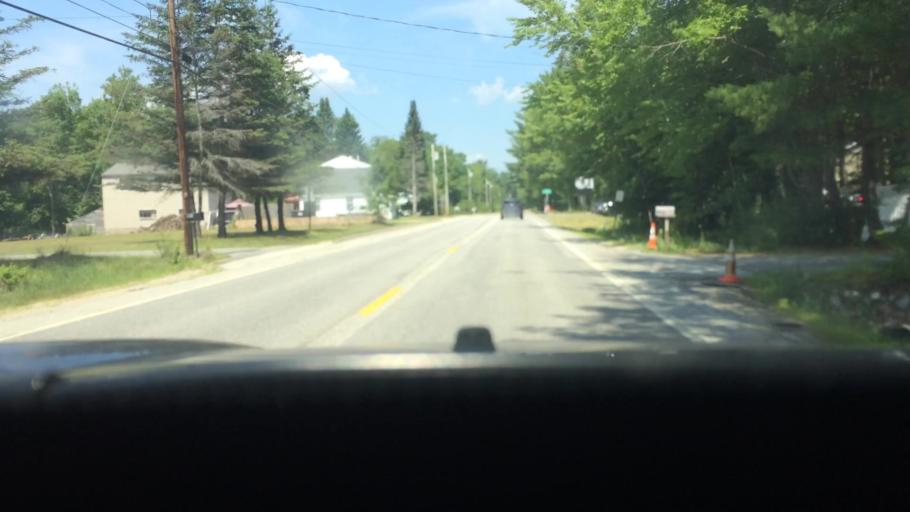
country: US
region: Maine
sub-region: Androscoggin County
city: Mechanic Falls
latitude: 44.1169
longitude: -70.4268
